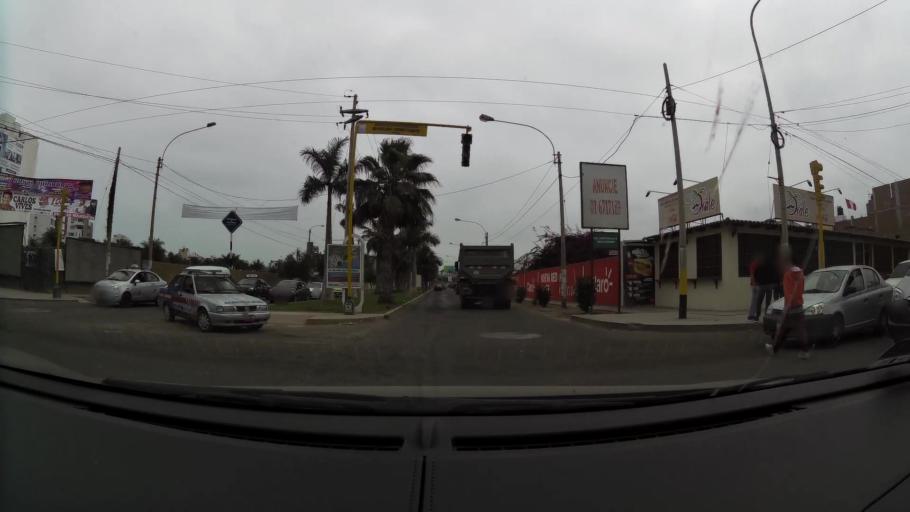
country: PE
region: La Libertad
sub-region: Provincia de Trujillo
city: Buenos Aires
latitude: -8.1350
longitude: -79.0366
